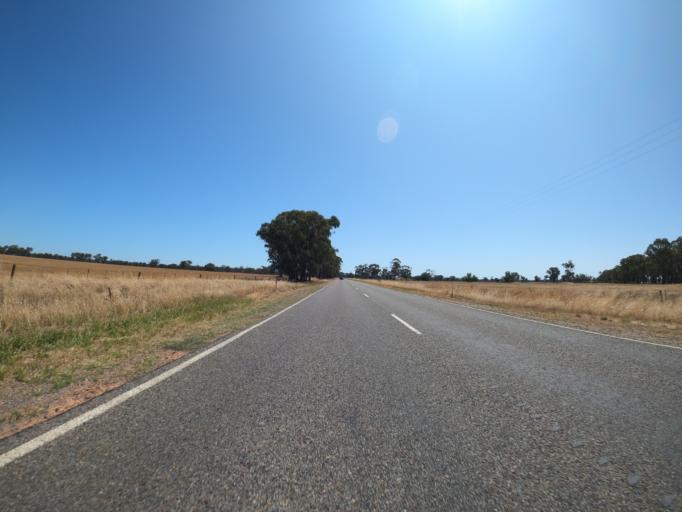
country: AU
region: New South Wales
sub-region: Corowa Shire
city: Corowa
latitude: -36.0655
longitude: 146.3745
